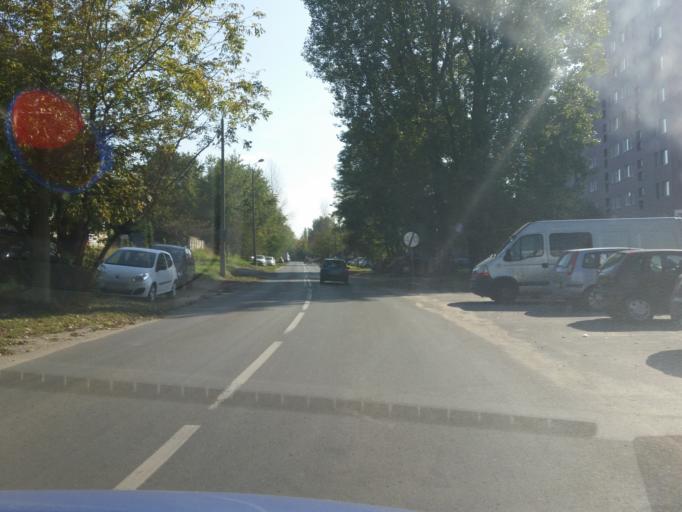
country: PL
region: Silesian Voivodeship
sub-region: Sosnowiec
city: Sosnowiec
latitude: 50.2682
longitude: 19.1249
